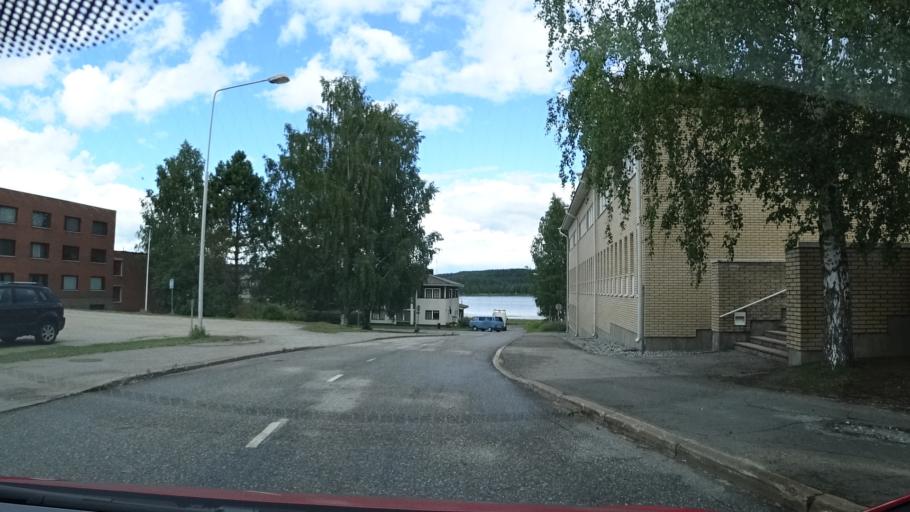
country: FI
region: North Karelia
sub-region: Pielisen Karjala
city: Nurmes
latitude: 63.5432
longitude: 29.1425
